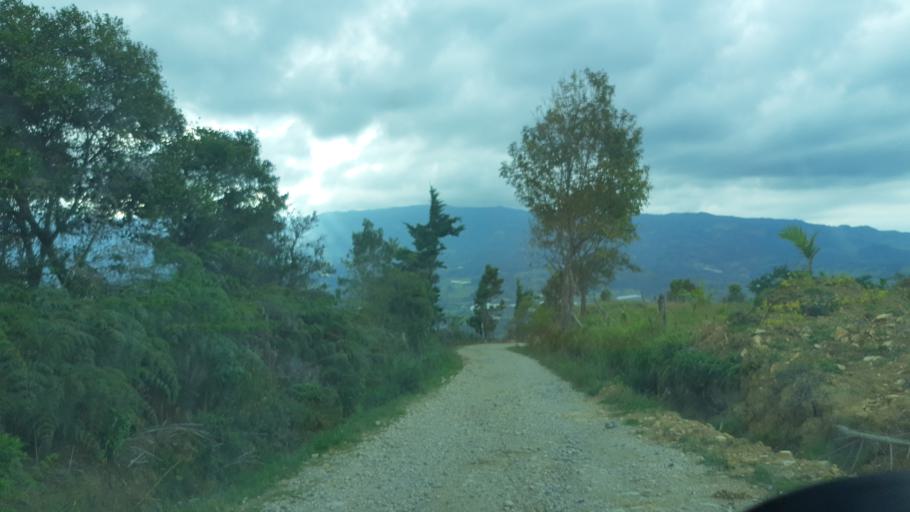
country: CO
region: Boyaca
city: Santa Sofia
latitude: 5.7453
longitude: -73.5651
